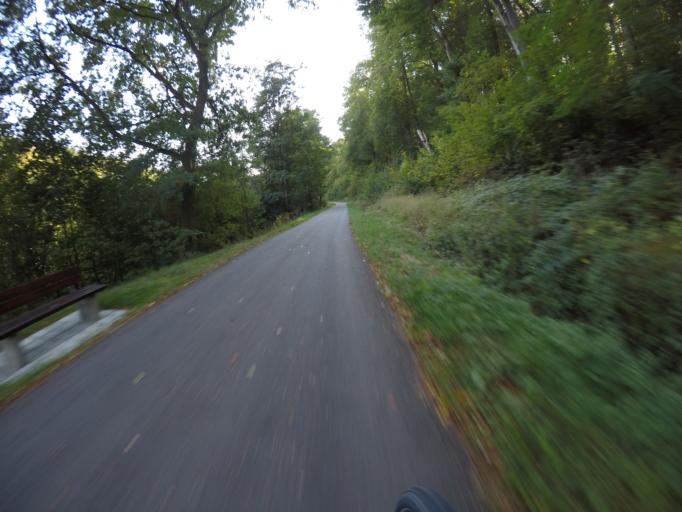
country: DE
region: Baden-Wuerttemberg
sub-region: Regierungsbezirk Stuttgart
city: Waldenbuch
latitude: 48.6416
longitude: 9.1671
